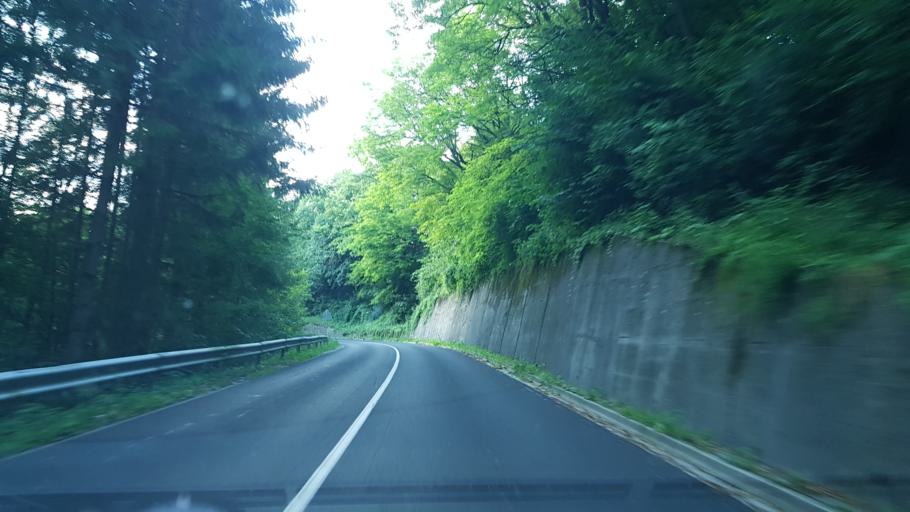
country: SI
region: Naklo
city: Naklo
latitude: 46.2537
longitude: 14.3169
